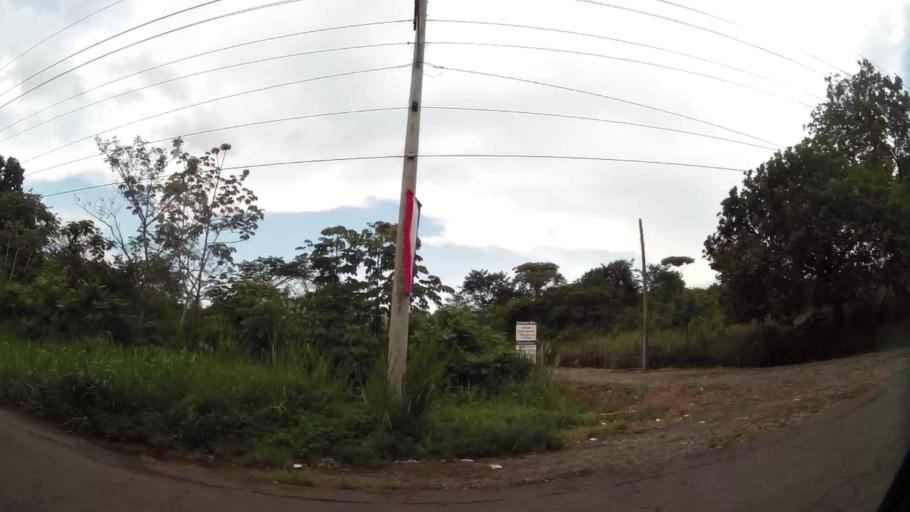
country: PA
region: Panama
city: Cabra Numero Uno
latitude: 9.1133
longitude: -79.3491
